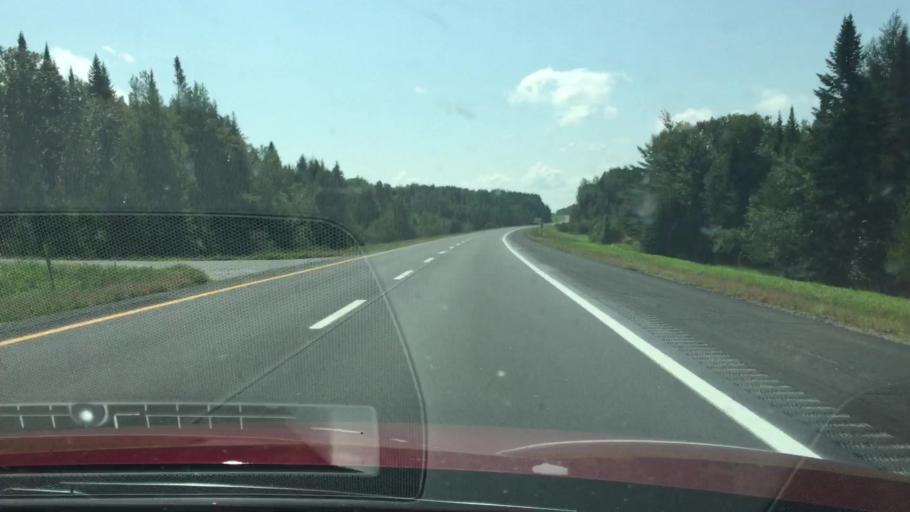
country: US
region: Maine
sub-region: Penobscot County
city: Patten
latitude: 45.9199
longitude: -68.3702
